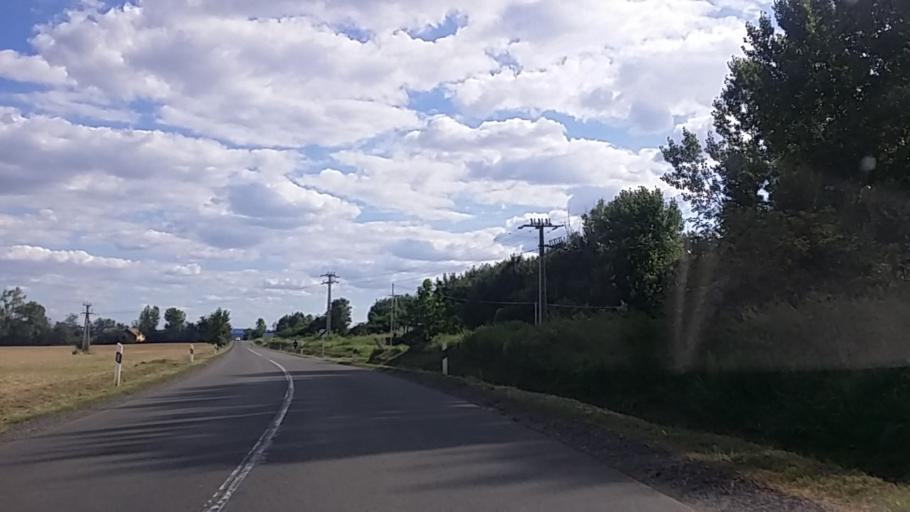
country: HU
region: Baranya
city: Sasd
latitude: 46.2717
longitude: 18.1037
